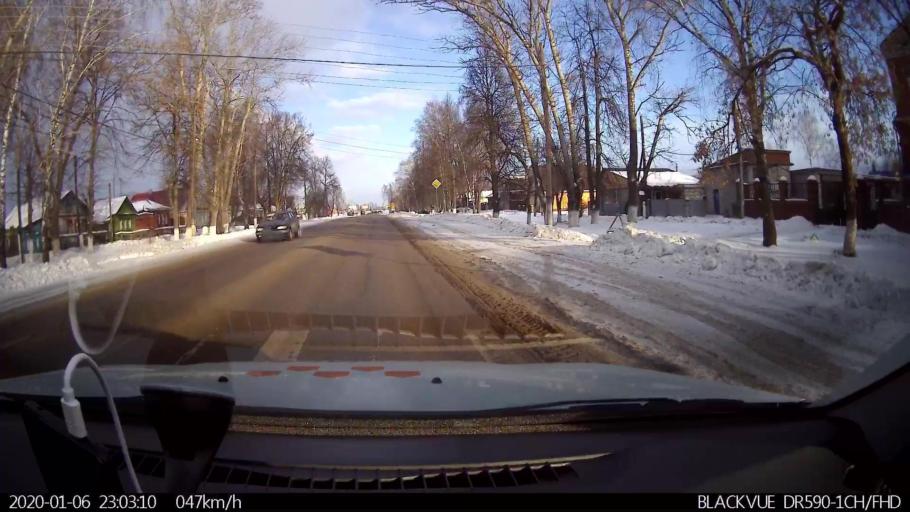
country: RU
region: Nizjnij Novgorod
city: Bogorodsk
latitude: 56.1113
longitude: 43.5319
